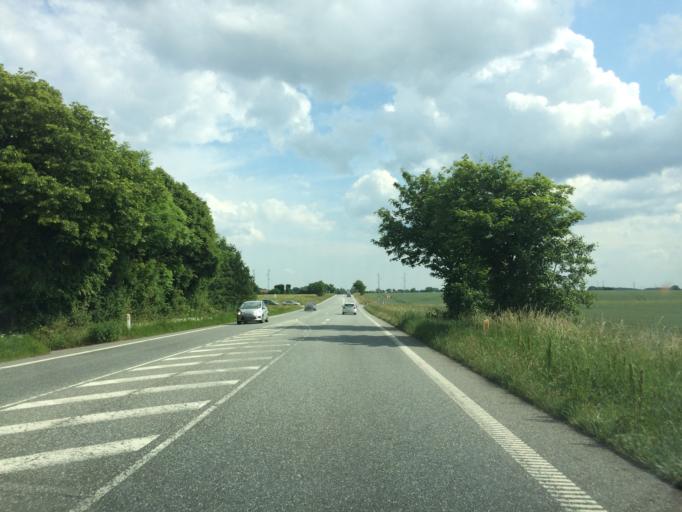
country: DK
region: South Denmark
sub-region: Fredericia Kommune
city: Taulov
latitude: 55.5722
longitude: 9.6650
